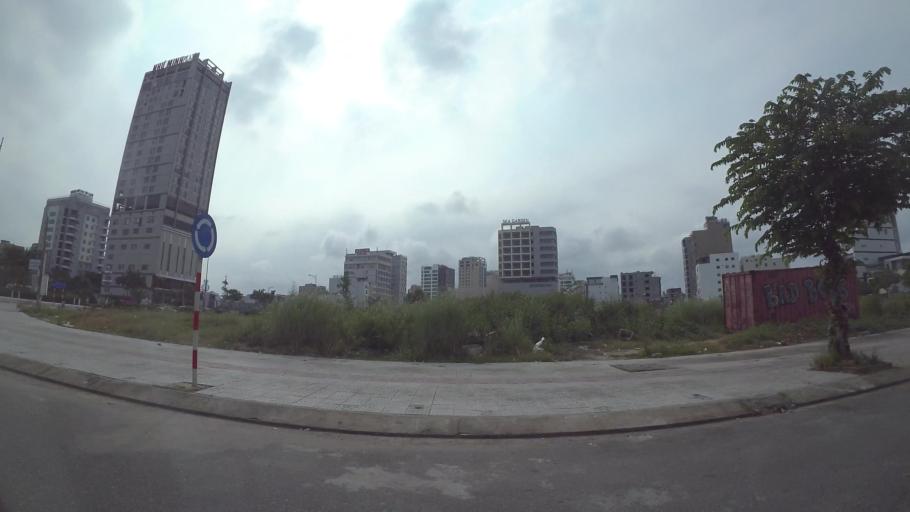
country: VN
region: Da Nang
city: Son Tra
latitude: 16.0706
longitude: 108.2397
